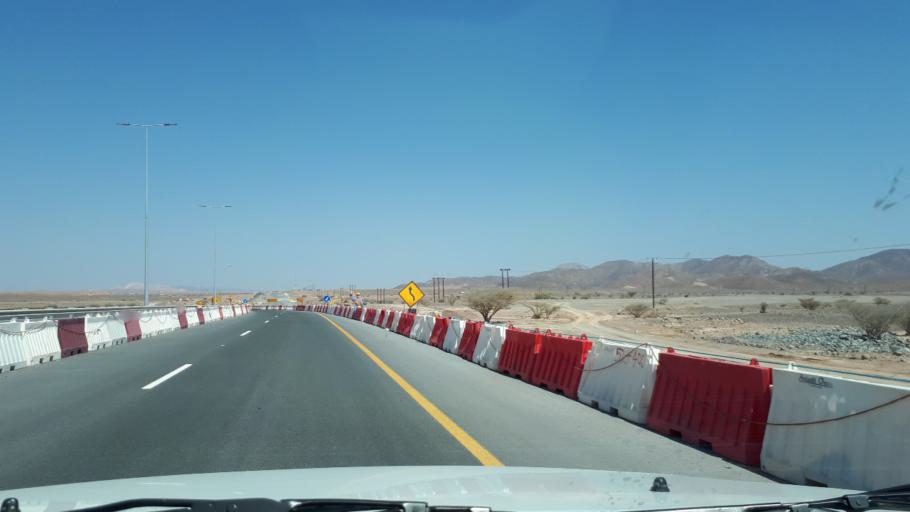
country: OM
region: Ash Sharqiyah
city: Badiyah
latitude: 22.4735
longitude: 58.9916
